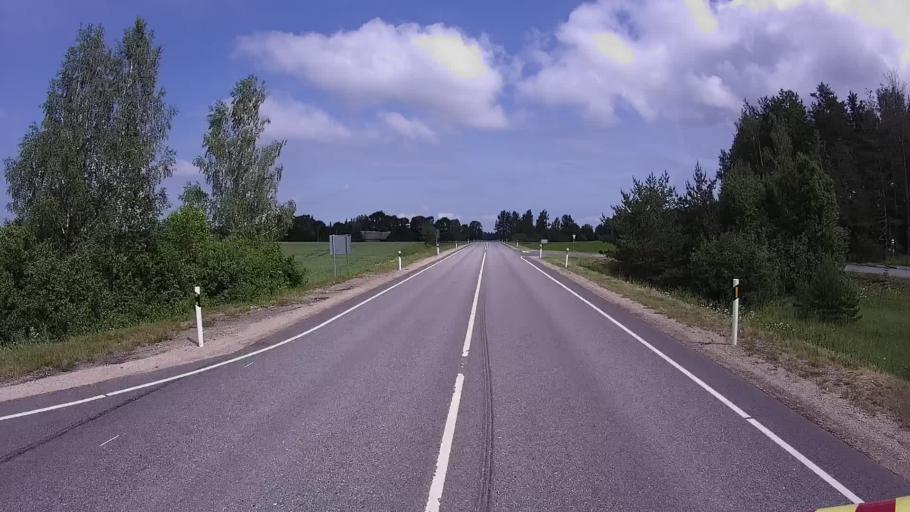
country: EE
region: Polvamaa
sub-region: Polva linn
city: Polva
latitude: 58.1244
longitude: 26.9554
